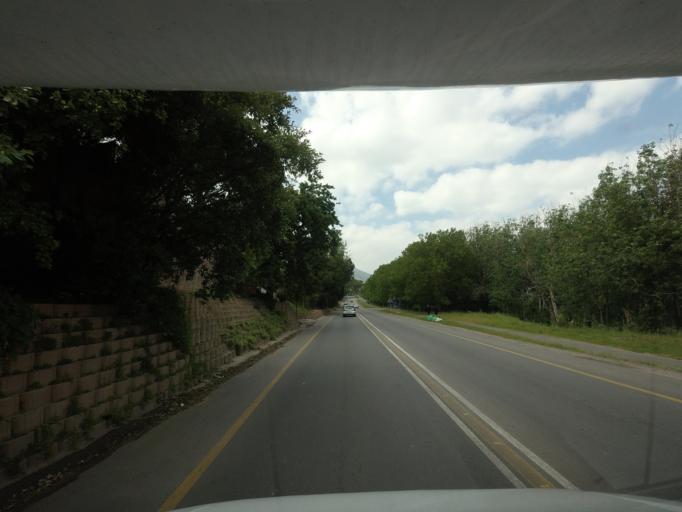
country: ZA
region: Western Cape
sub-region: City of Cape Town
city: Constantia
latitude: -34.0360
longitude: 18.3568
